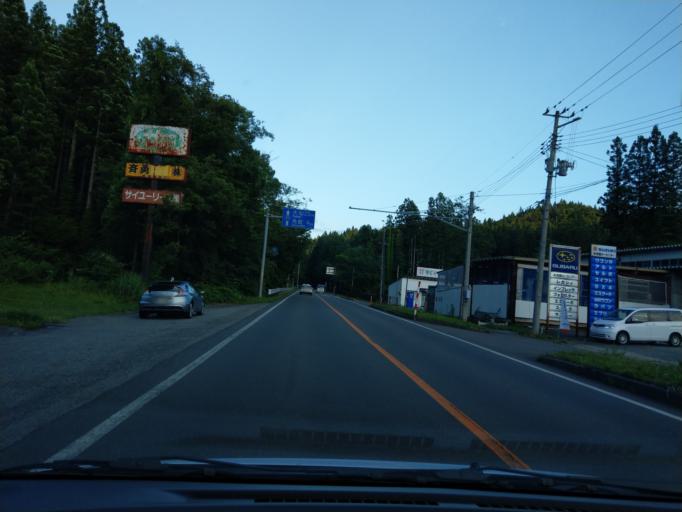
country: JP
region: Akita
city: Kakunodatemachi
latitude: 39.6048
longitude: 140.5693
